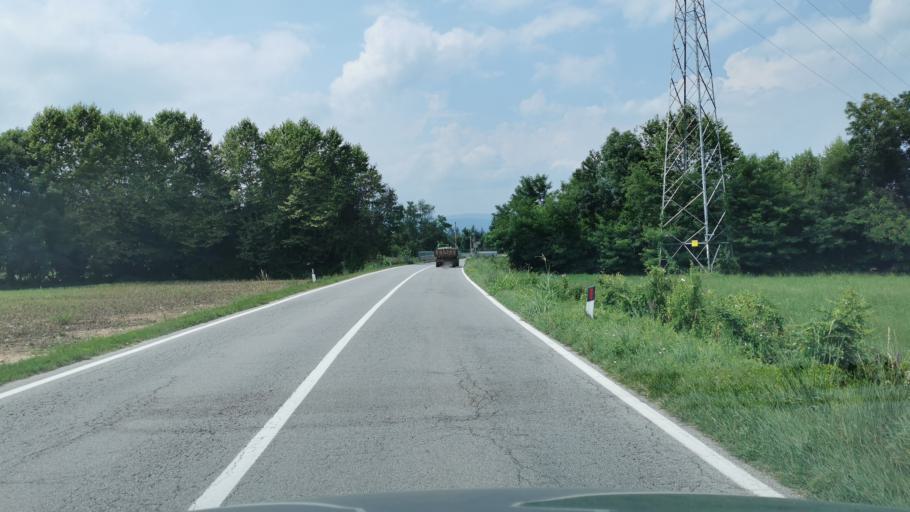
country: IT
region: Piedmont
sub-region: Provincia di Cuneo
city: Roata Rossi
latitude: 44.4352
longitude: 7.4998
